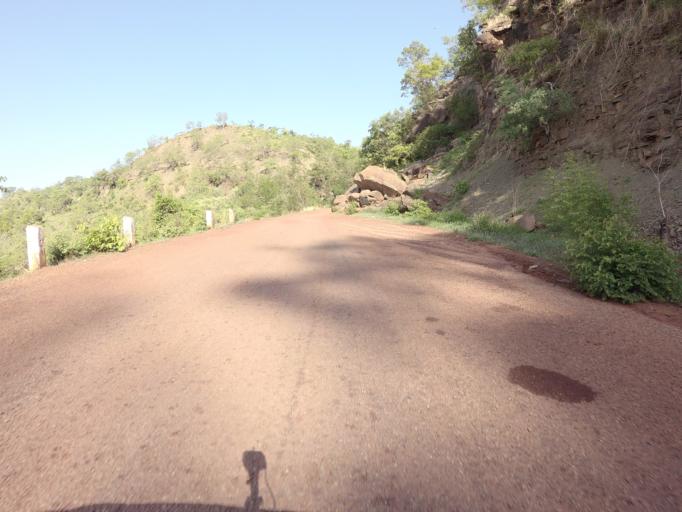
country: GH
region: Upper East
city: Bawku
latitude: 10.6421
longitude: -0.1955
